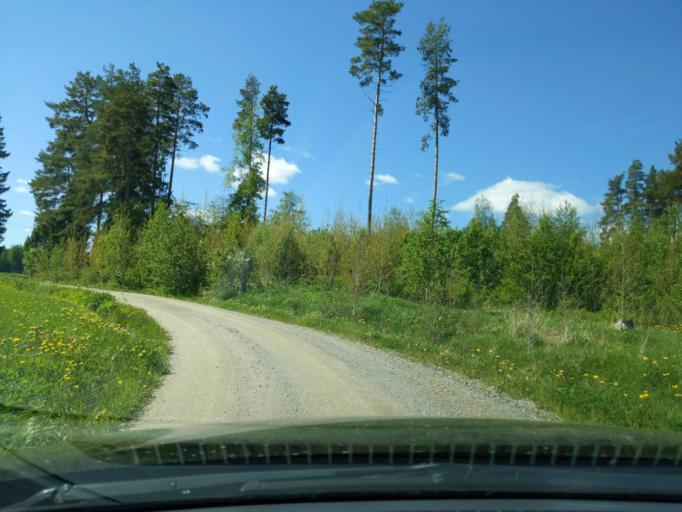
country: FI
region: Paijanne Tavastia
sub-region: Lahti
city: Lahti
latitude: 61.0575
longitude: 25.6762
